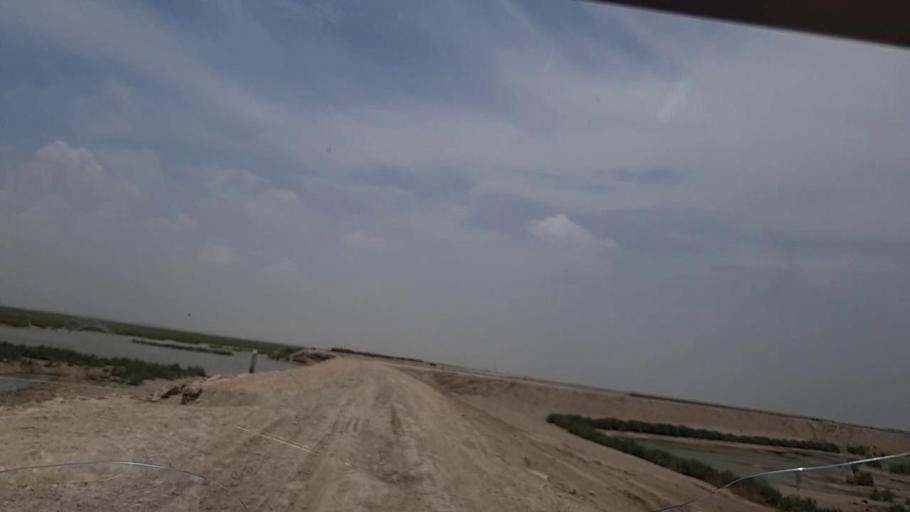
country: PK
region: Sindh
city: Bhan
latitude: 26.5089
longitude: 67.6269
